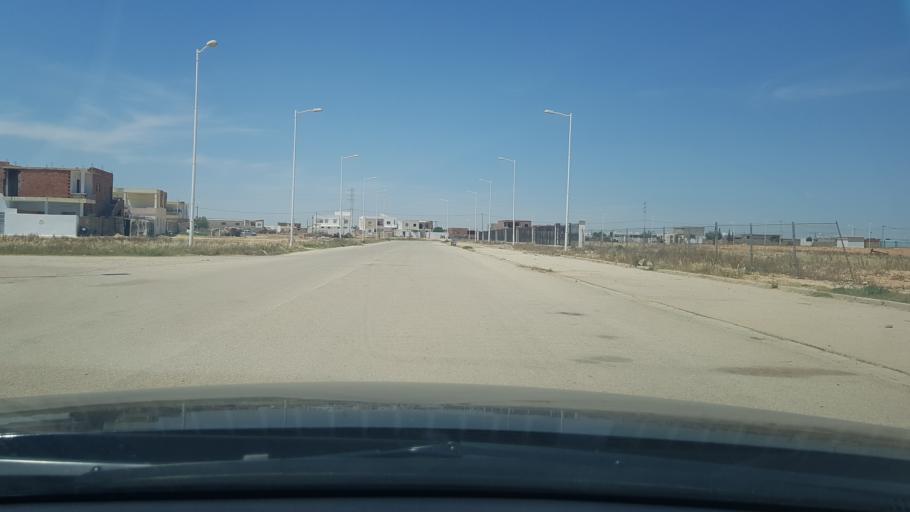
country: TN
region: Safaqis
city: Al Qarmadah
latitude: 34.8348
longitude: 10.7492
